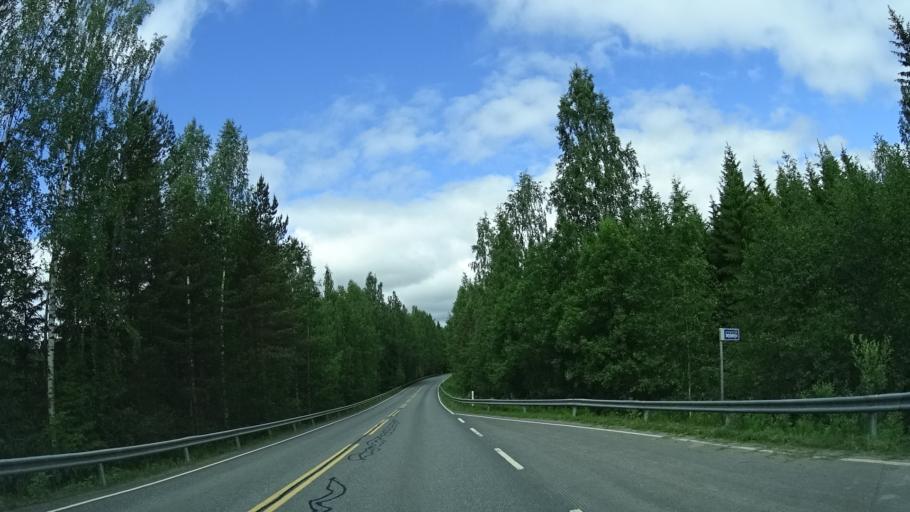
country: FI
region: Central Finland
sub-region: Jyvaeskylae
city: Korpilahti
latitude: 62.0167
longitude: 25.6418
